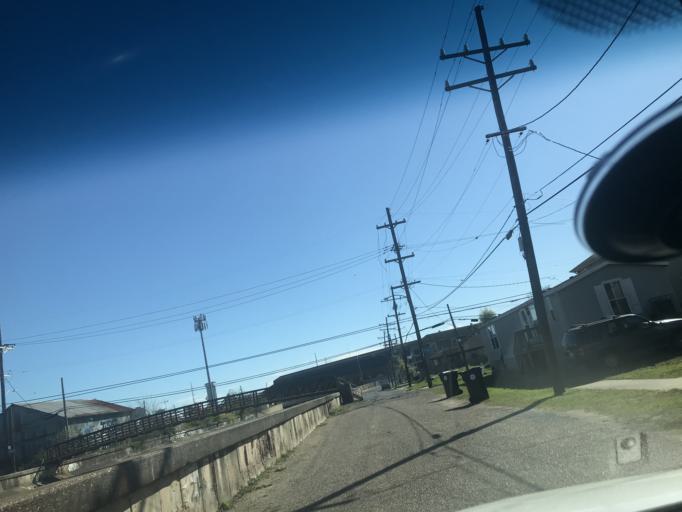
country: US
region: Louisiana
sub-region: Orleans Parish
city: New Orleans
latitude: 29.9530
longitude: -90.1005
